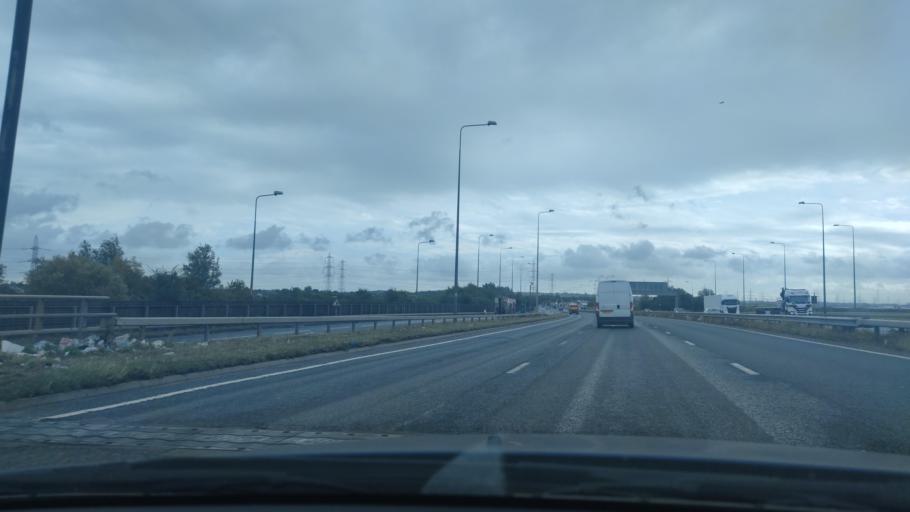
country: GB
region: England
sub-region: Greater London
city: Erith
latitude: 51.5113
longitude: 0.1874
